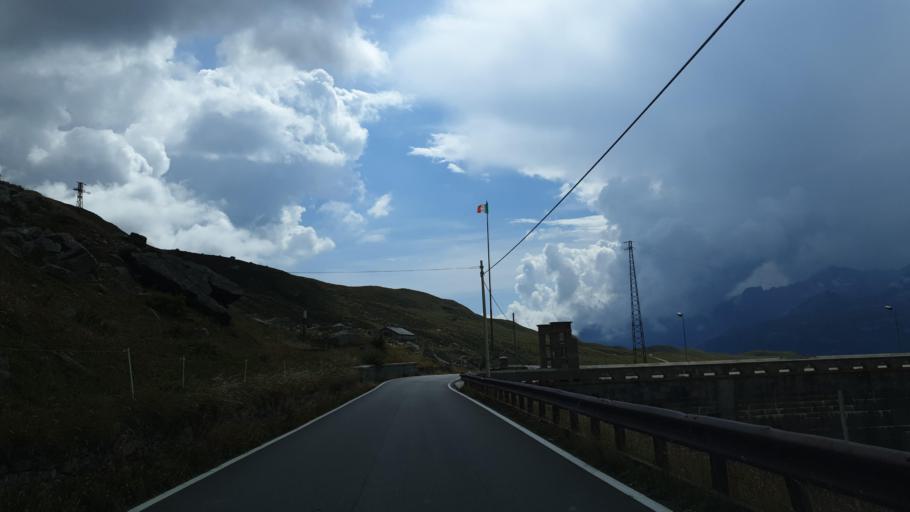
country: IT
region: Lombardy
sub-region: Provincia di Sondrio
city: Campodolcino
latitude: 46.4716
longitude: 9.3516
